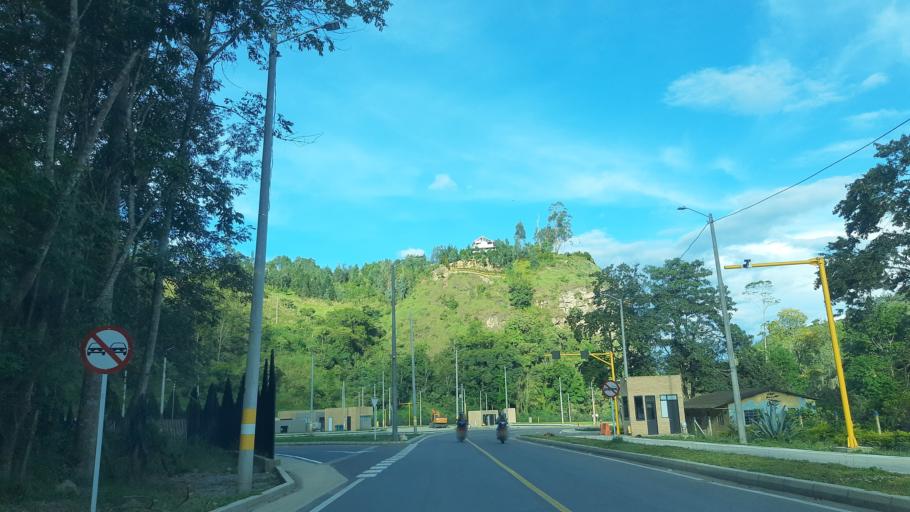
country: CO
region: Cundinamarca
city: Macheta
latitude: 5.0751
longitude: -73.5855
